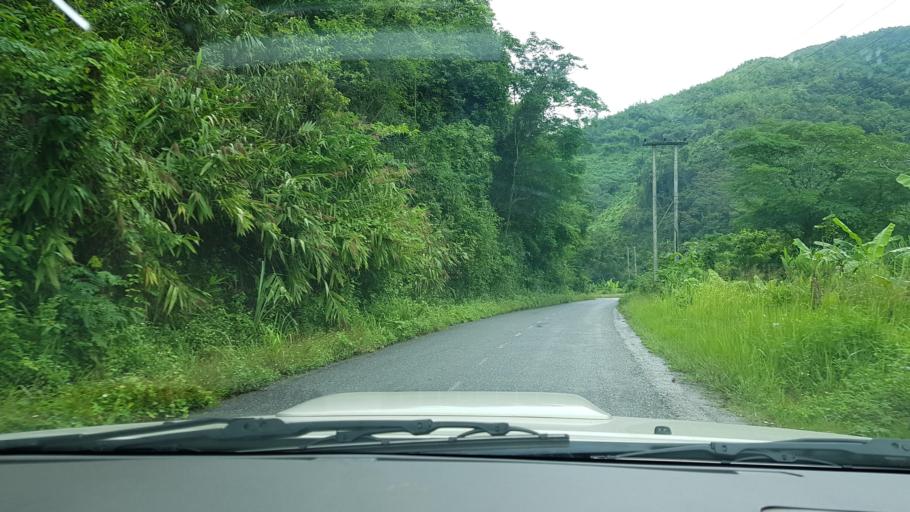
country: LA
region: Phongsali
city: Khoa
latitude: 21.1023
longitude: 102.2789
